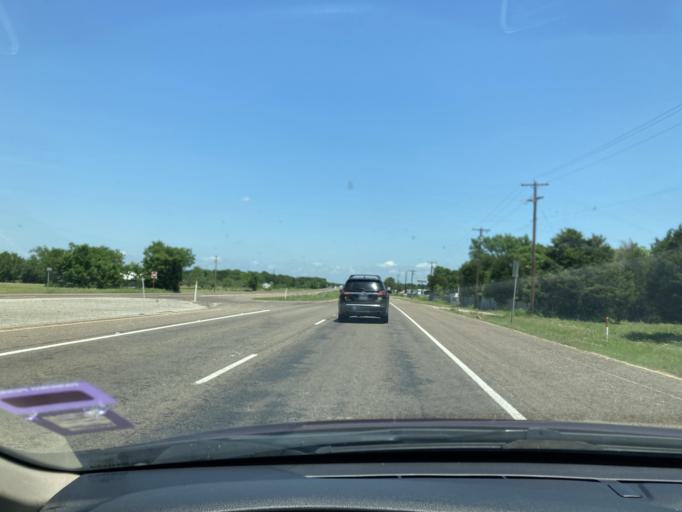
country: US
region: Texas
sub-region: Navarro County
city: Kerens
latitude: 32.1348
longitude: -96.2183
